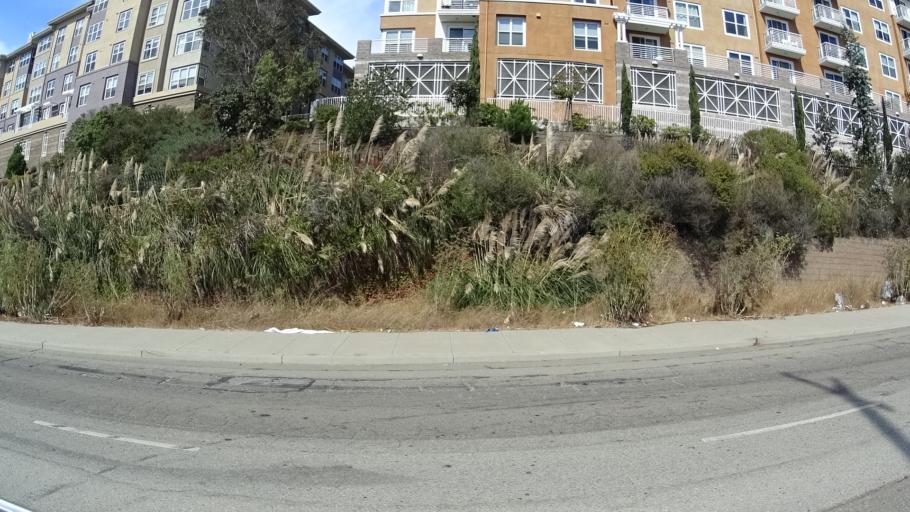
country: US
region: California
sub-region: San Mateo County
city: Brisbane
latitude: 37.7105
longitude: -122.3886
